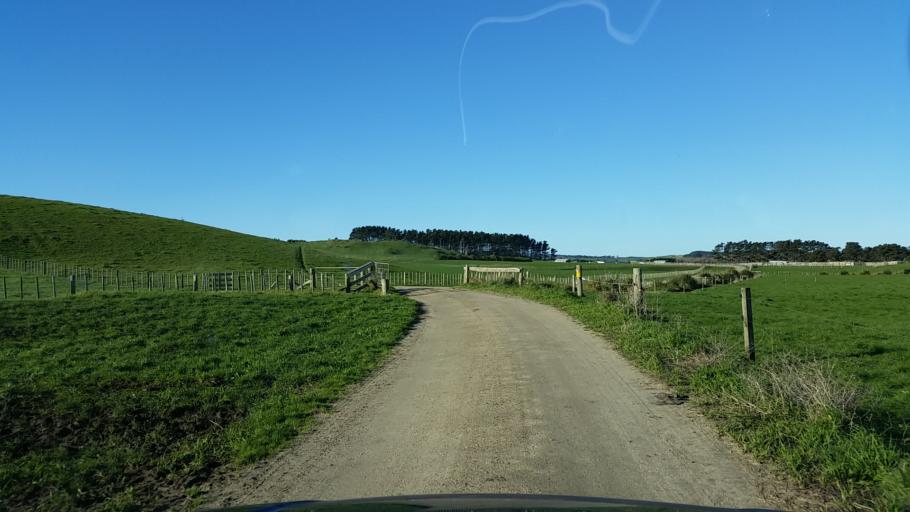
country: NZ
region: Taranaki
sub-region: South Taranaki District
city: Patea
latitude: -39.8377
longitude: 174.6957
